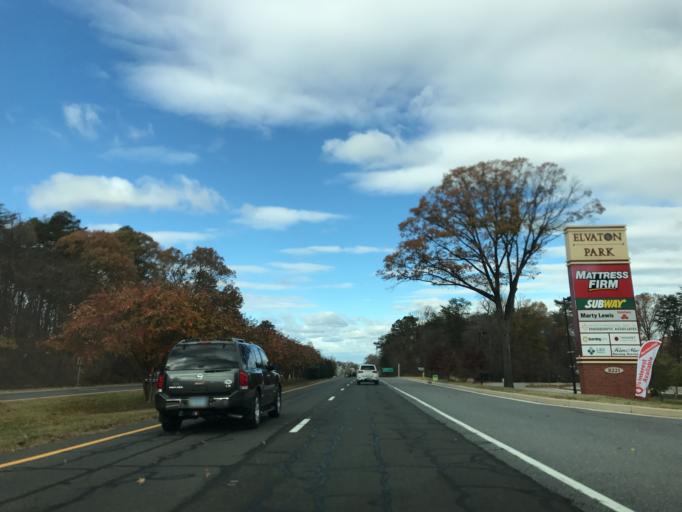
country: US
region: Maryland
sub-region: Anne Arundel County
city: Pasadena
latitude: 39.1164
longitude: -76.5808
